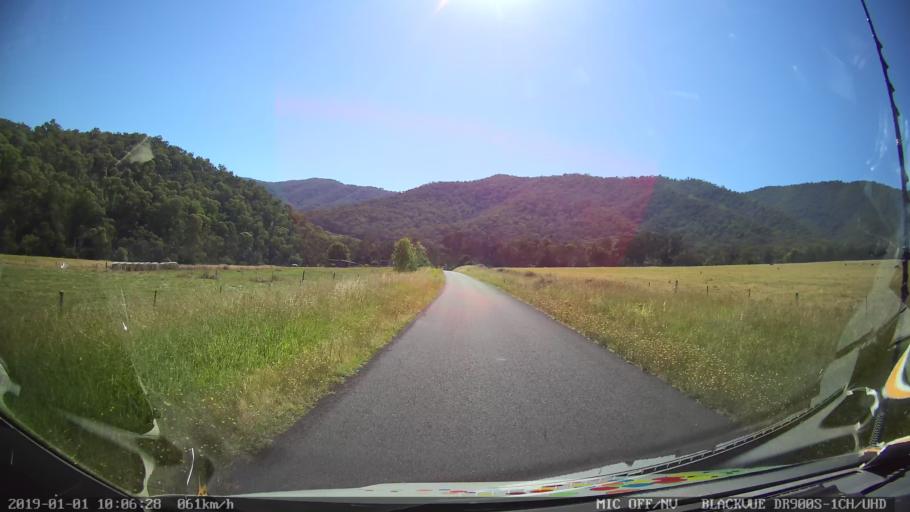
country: AU
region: New South Wales
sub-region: Snowy River
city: Jindabyne
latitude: -36.1746
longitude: 148.1485
